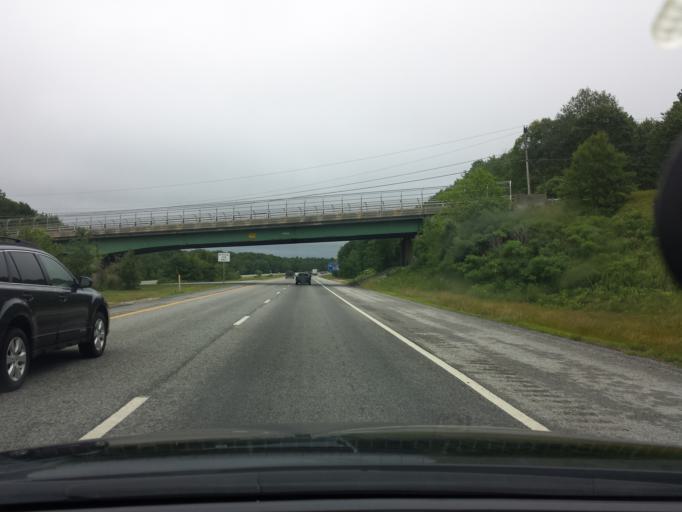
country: US
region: Rhode Island
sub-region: Kent County
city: West Greenwich
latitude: 41.5916
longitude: -71.6594
